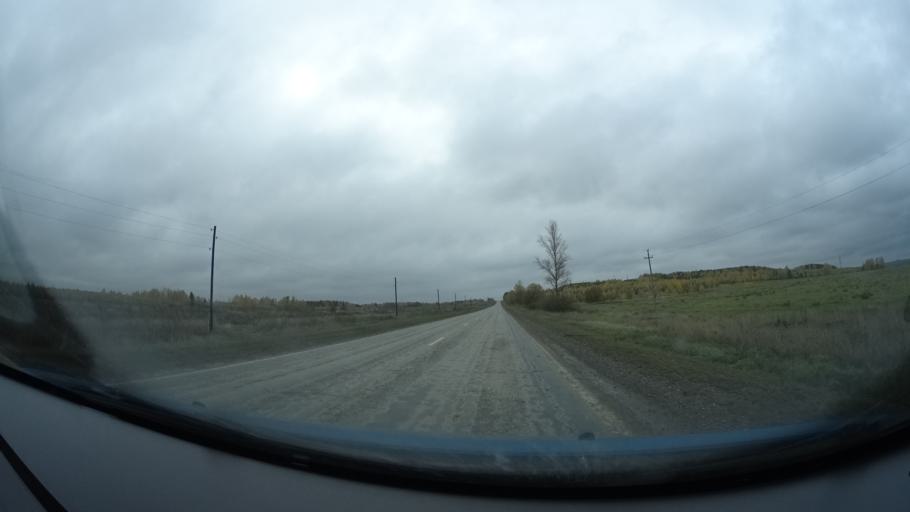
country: RU
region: Perm
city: Osa
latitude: 57.1366
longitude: 55.5271
